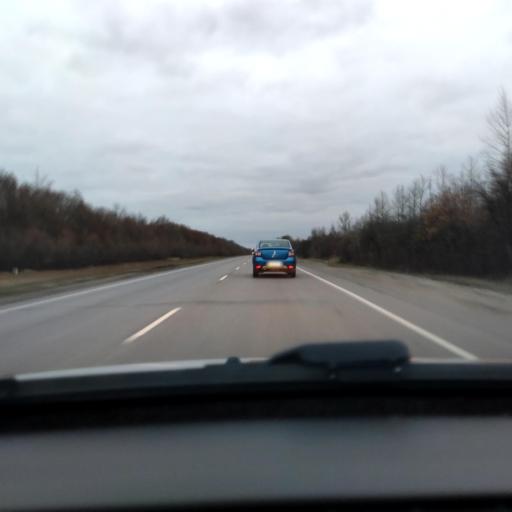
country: RU
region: Lipetsk
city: Borinskoye
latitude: 52.4282
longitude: 39.2634
